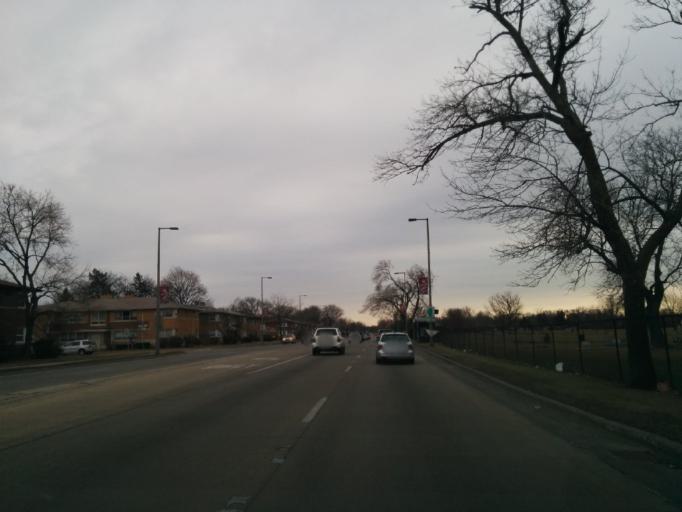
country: US
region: Illinois
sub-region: Cook County
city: Westchester
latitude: 41.8612
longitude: -87.8825
